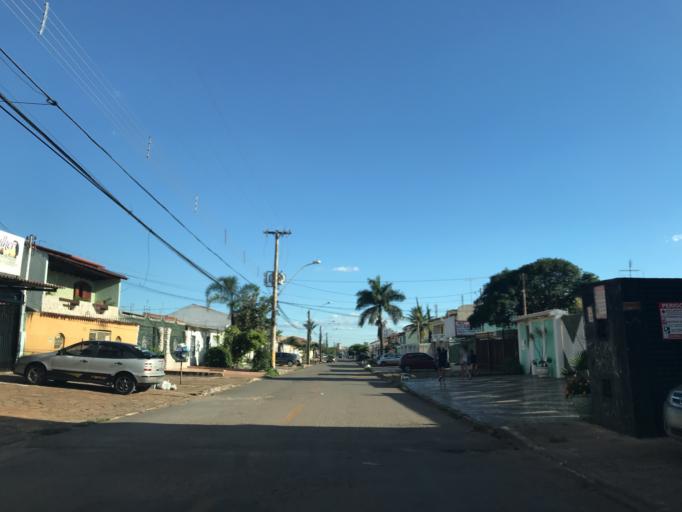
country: BR
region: Federal District
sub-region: Brasilia
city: Brasilia
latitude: -15.8114
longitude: -48.0638
